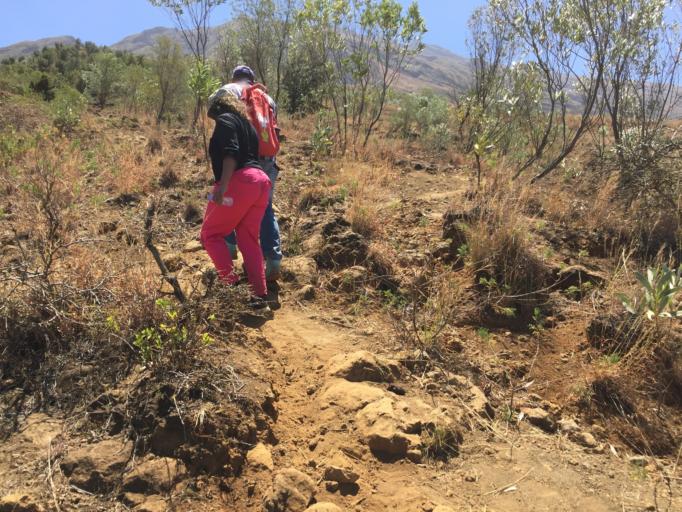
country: CV
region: Mosteiros
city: Porto dos Mosteiros
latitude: 15.0084
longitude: -24.3822
